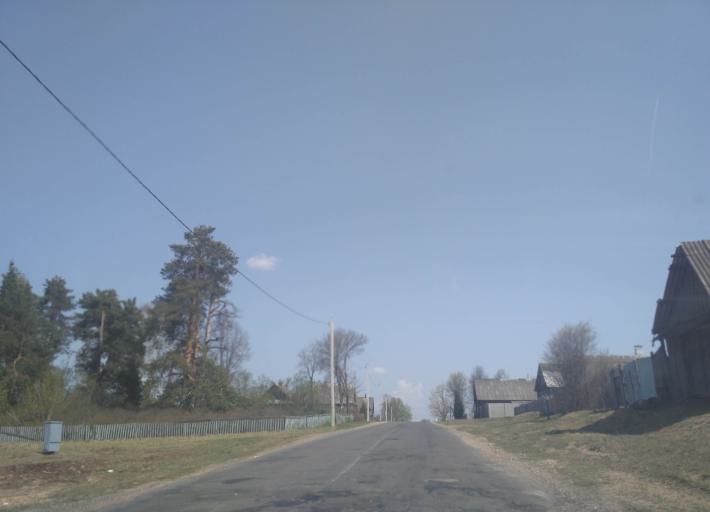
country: BY
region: Minsk
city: Loshnitsa
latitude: 54.4054
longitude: 28.6213
